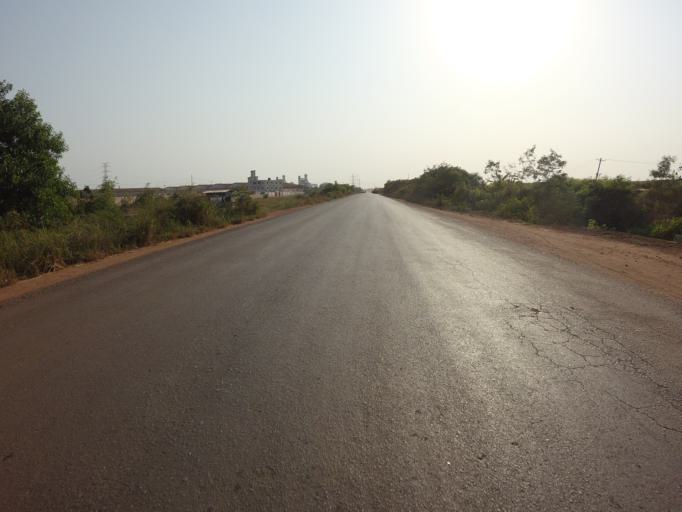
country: GH
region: Greater Accra
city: Tema
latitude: 5.6880
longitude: 0.0455
